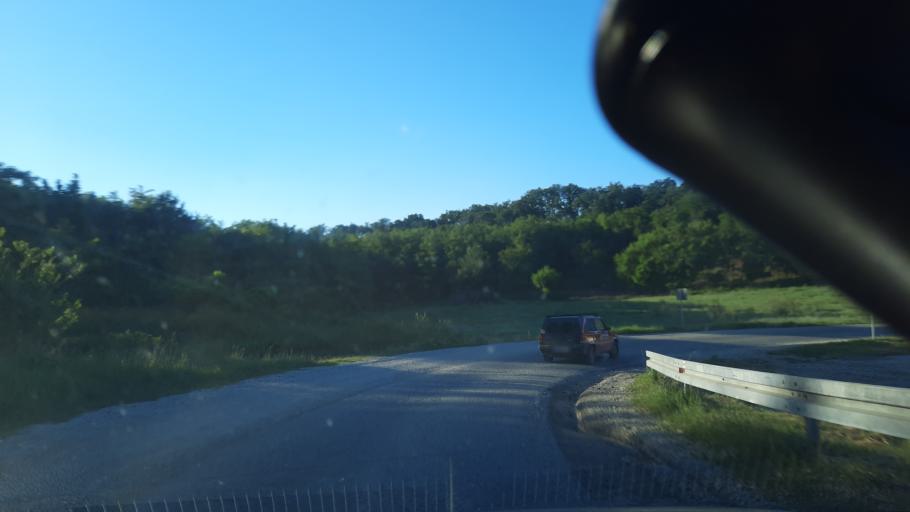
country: RS
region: Autonomna Pokrajina Vojvodina
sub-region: Juznobacki Okrug
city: Sremski Karlovci
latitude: 45.1214
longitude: 19.9382
